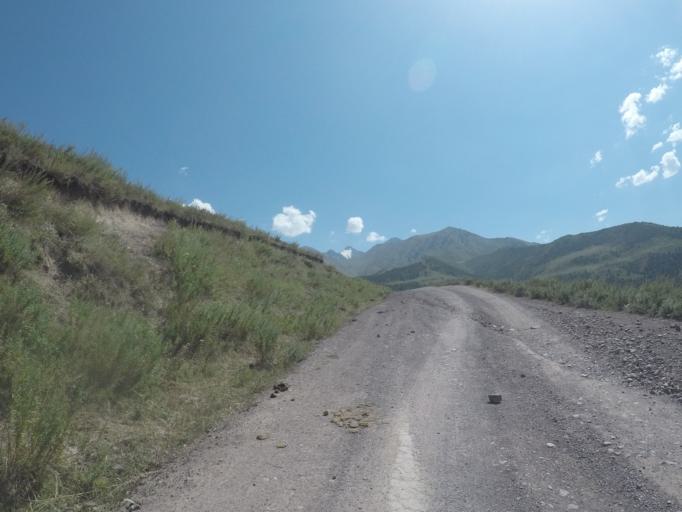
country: KG
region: Chuy
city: Bishkek
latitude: 42.6490
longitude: 74.5212
